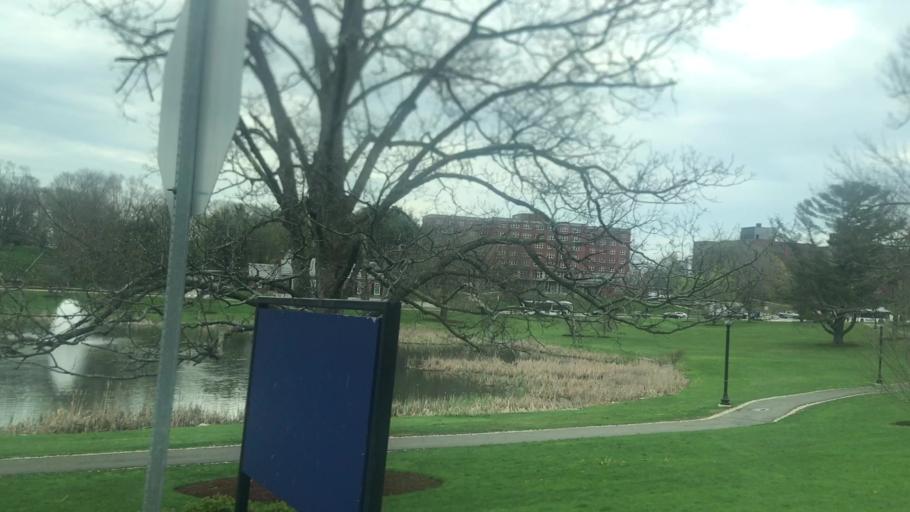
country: US
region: Connecticut
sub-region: Tolland County
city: Storrs
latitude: 41.8061
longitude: -72.2478
